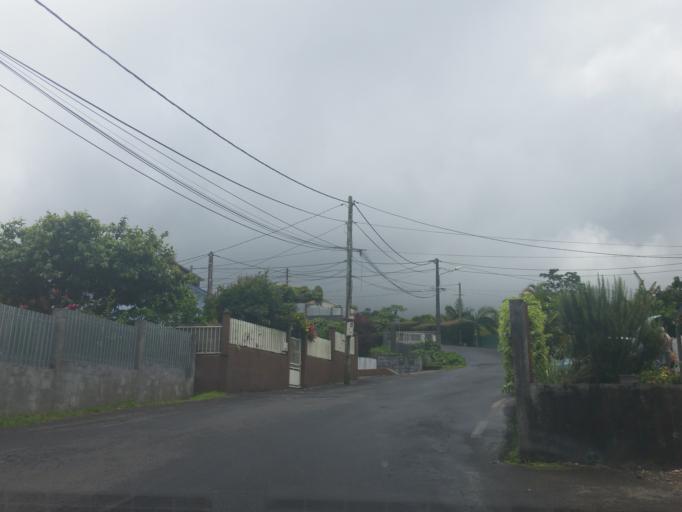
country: RE
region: Reunion
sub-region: Reunion
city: Le Tampon
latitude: -21.2427
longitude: 55.5133
